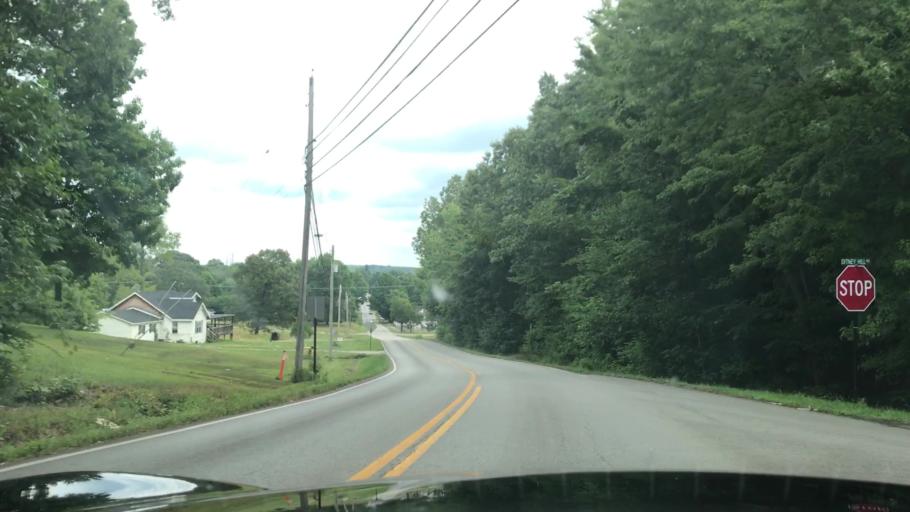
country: US
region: Kentucky
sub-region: Muhlenberg County
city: Central City
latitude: 37.2138
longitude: -87.0577
